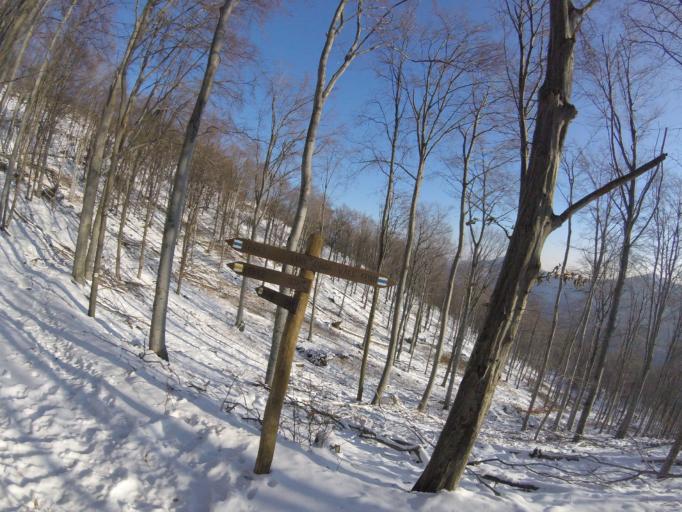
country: HU
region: Heves
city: Parad
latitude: 47.8750
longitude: 20.0425
